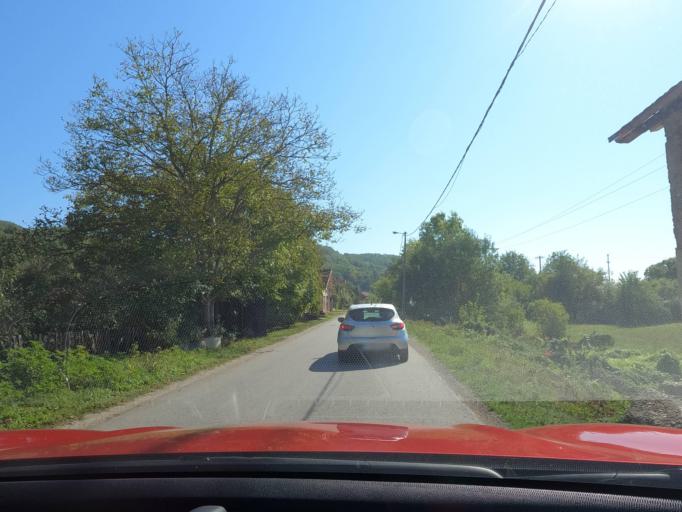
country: RS
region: Central Serbia
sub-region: Raski Okrug
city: Kraljevo
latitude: 43.7402
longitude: 20.7337
